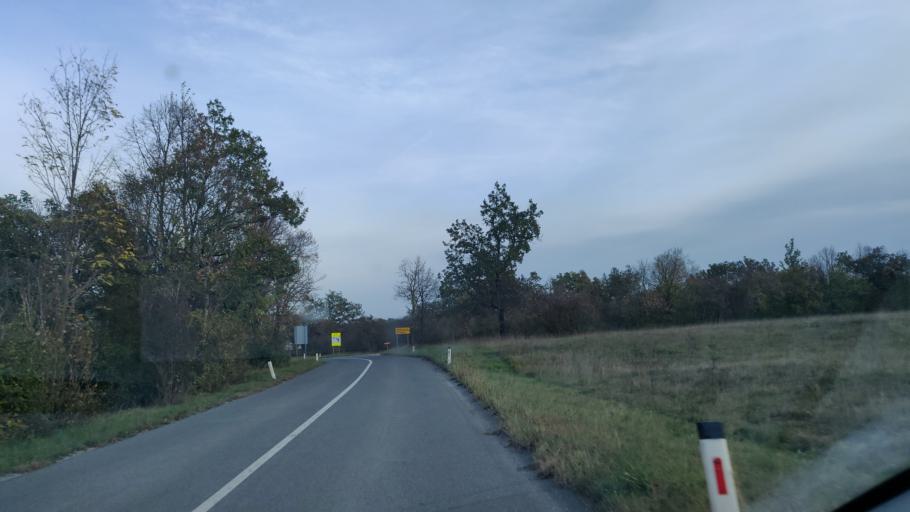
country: SI
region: Komen
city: Komen
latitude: 45.8133
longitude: 13.7952
